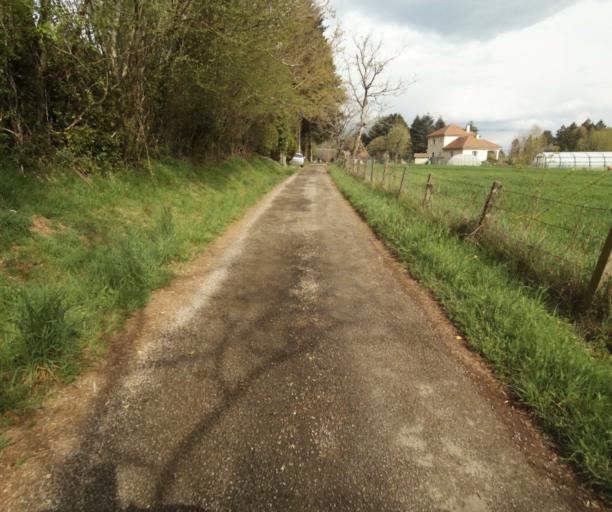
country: FR
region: Limousin
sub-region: Departement de la Correze
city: Tulle
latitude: 45.2888
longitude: 1.7413
